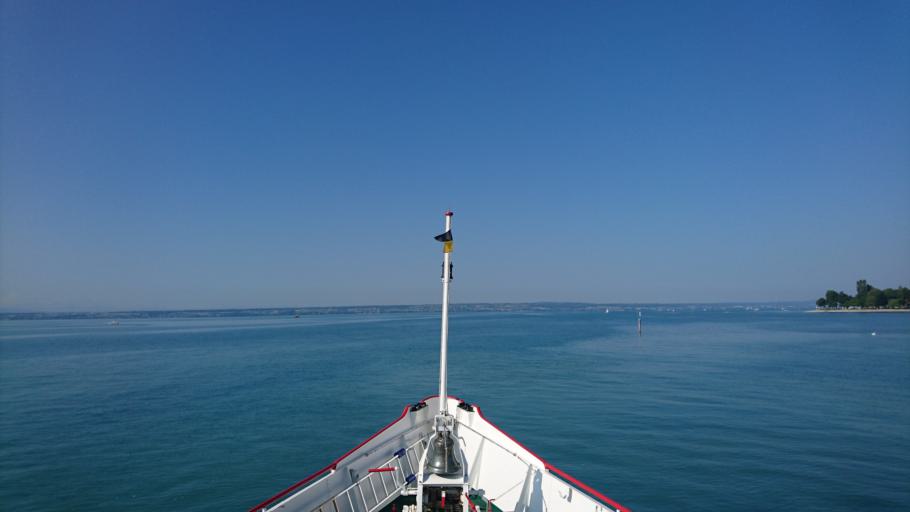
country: DE
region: Baden-Wuerttemberg
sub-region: Tuebingen Region
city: Immenstaad am Bodensee
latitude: 47.6607
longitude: 9.3674
